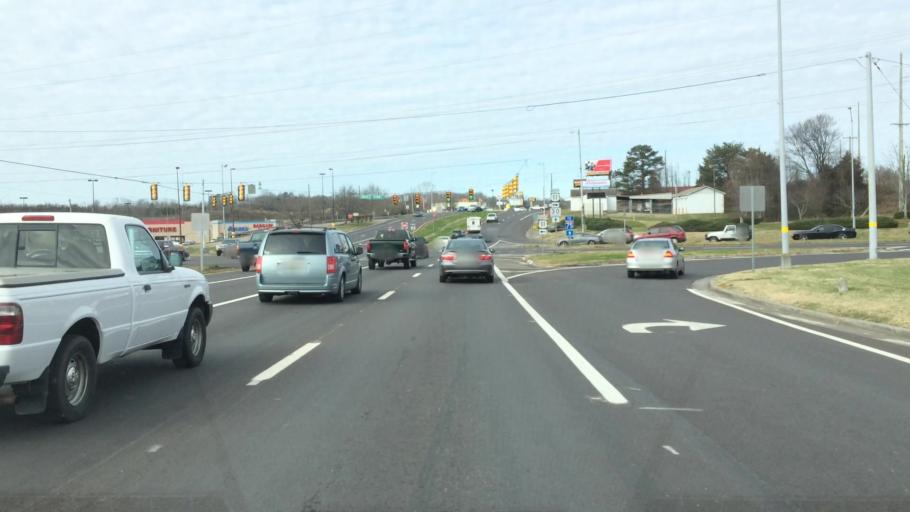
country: US
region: Tennessee
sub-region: McMinn County
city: Athens
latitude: 35.4507
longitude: -84.6225
